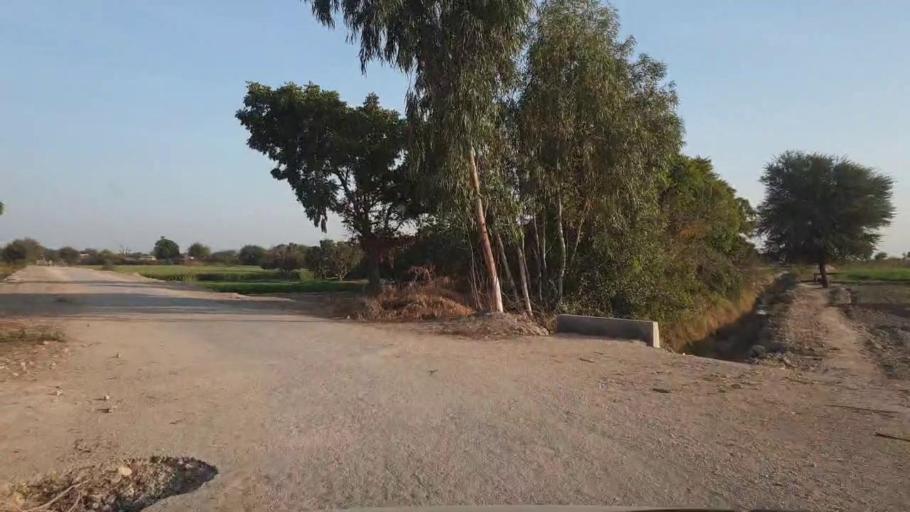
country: PK
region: Sindh
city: Chambar
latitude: 25.2584
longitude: 68.8034
